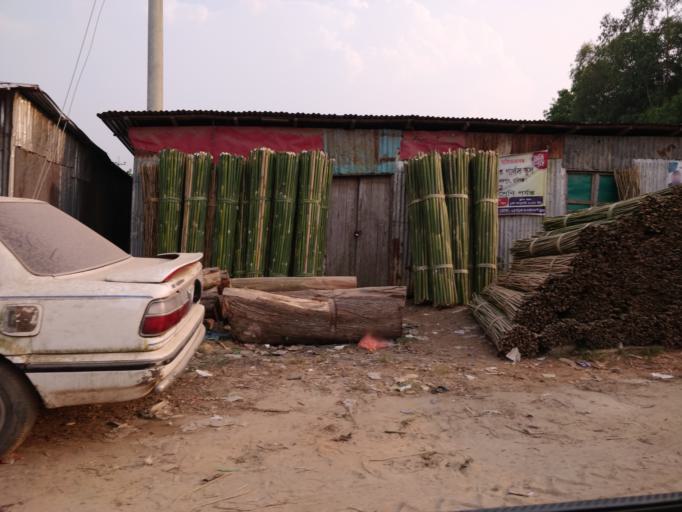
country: BD
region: Sylhet
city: Habiganj
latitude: 24.1487
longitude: 91.3509
